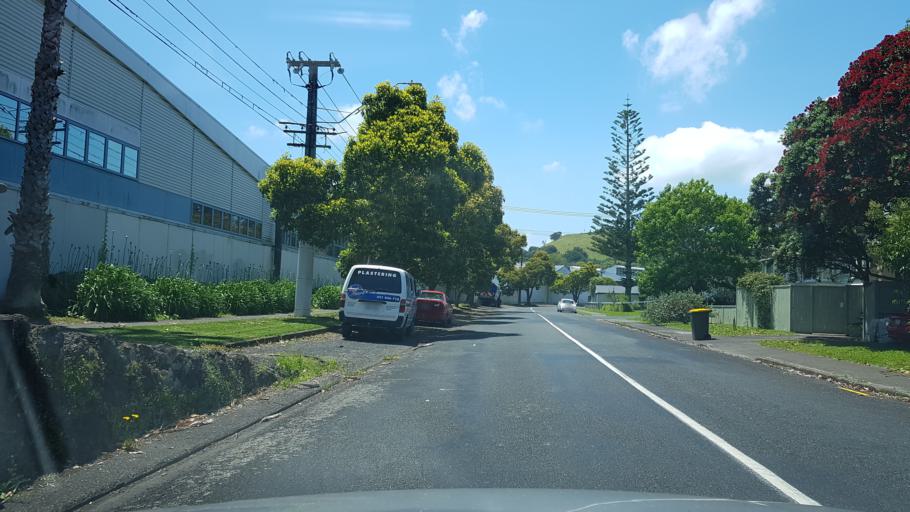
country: NZ
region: Auckland
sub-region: Auckland
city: Auckland
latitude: -36.8257
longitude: 174.7895
